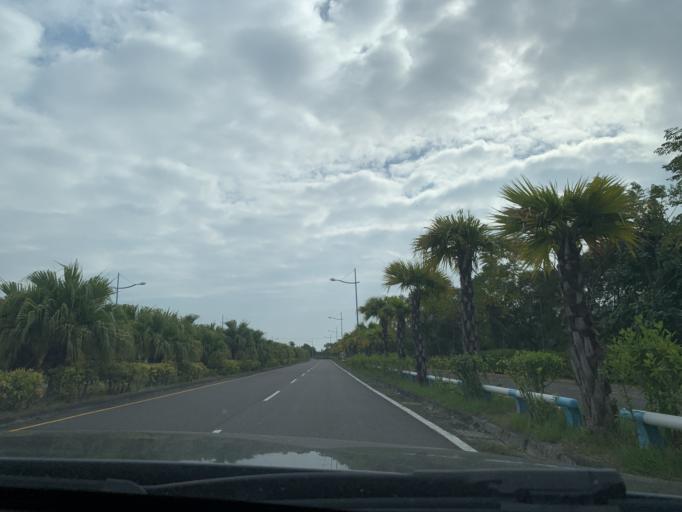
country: TW
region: Taiwan
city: Fengshan
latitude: 22.4472
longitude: 120.4877
